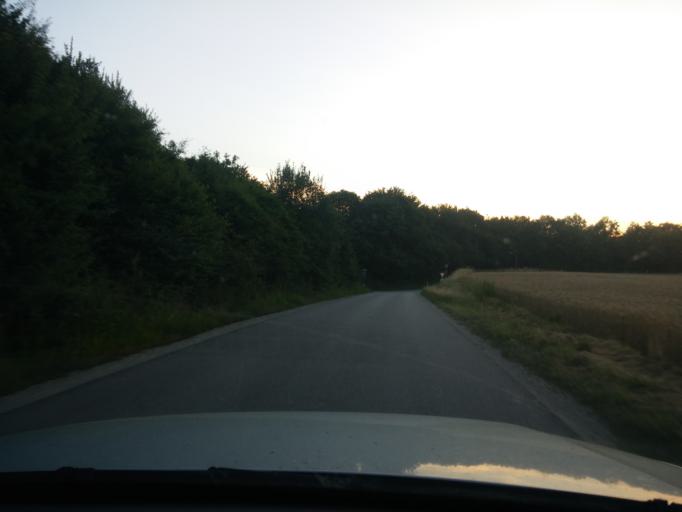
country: DE
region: Bavaria
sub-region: Upper Bavaria
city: Feldkirchen
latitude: 48.1430
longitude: 11.7625
